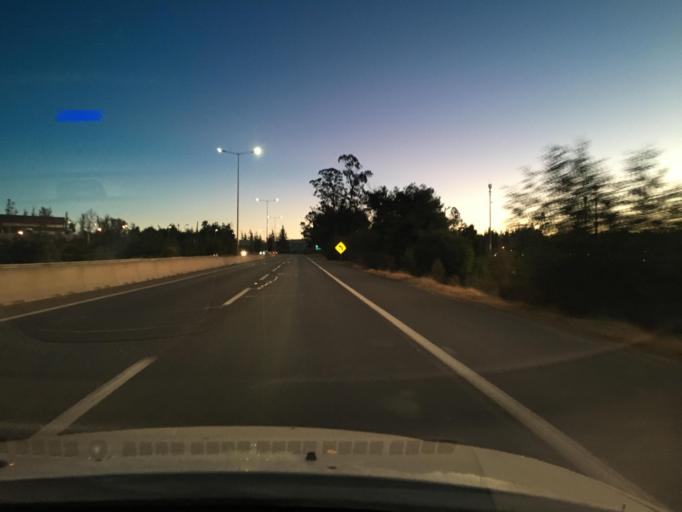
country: CL
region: Valparaiso
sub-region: Provincia de Valparaiso
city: Vina del Mar
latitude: -33.1364
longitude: -71.5628
